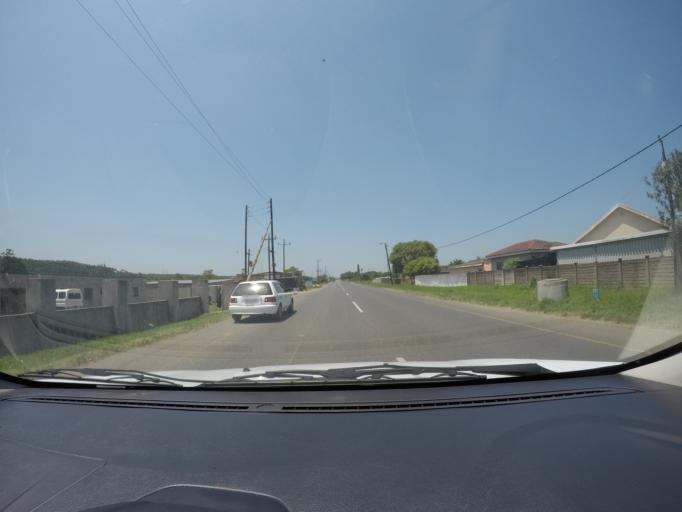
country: ZA
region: KwaZulu-Natal
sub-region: uThungulu District Municipality
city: eSikhawini
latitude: -28.8866
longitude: 31.8844
